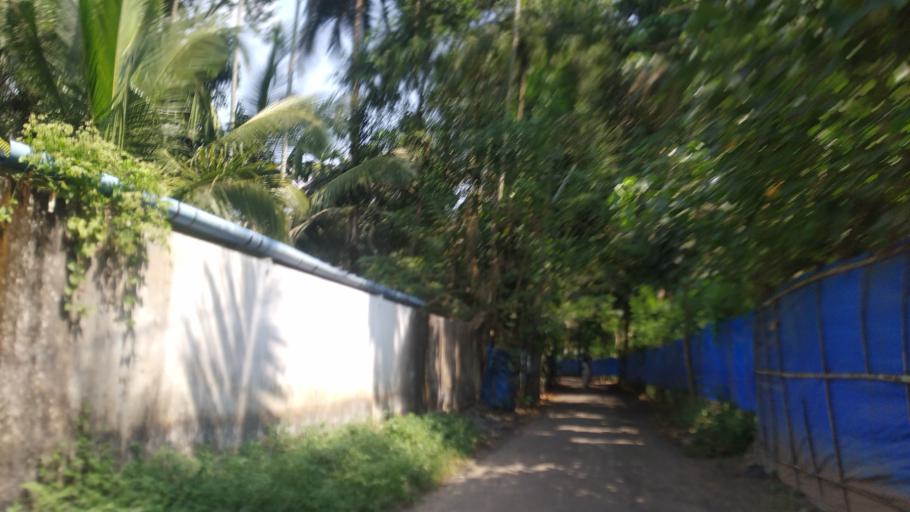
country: IN
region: Kerala
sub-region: Ernakulam
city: Elur
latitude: 10.1223
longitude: 76.2349
